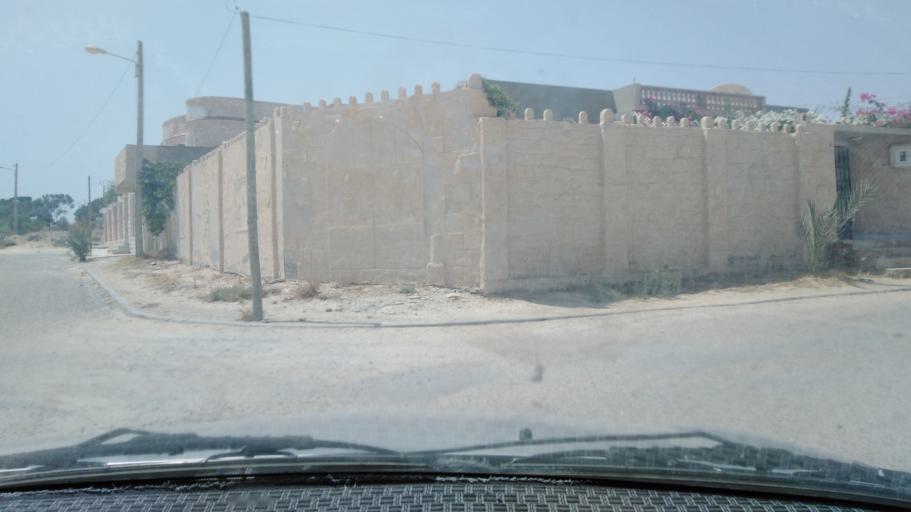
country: TN
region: Qabis
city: Gabes
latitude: 33.9541
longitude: 9.9988
